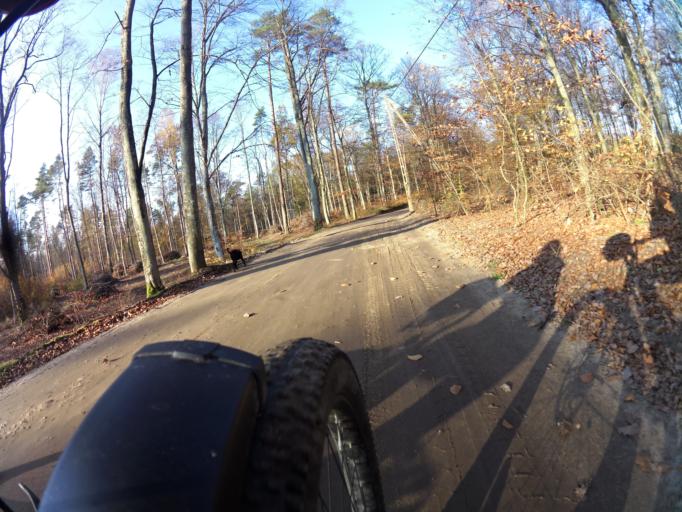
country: PL
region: Pomeranian Voivodeship
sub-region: Powiat pucki
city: Krokowa
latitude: 54.7282
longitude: 18.2075
